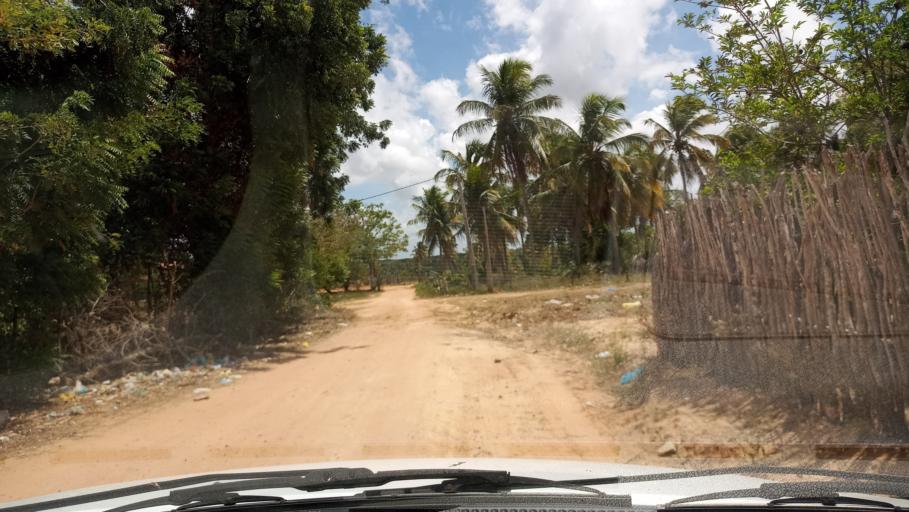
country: BR
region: Rio Grande do Norte
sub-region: Maxaranguape
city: Sao Miguel
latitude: -5.4824
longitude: -35.3306
